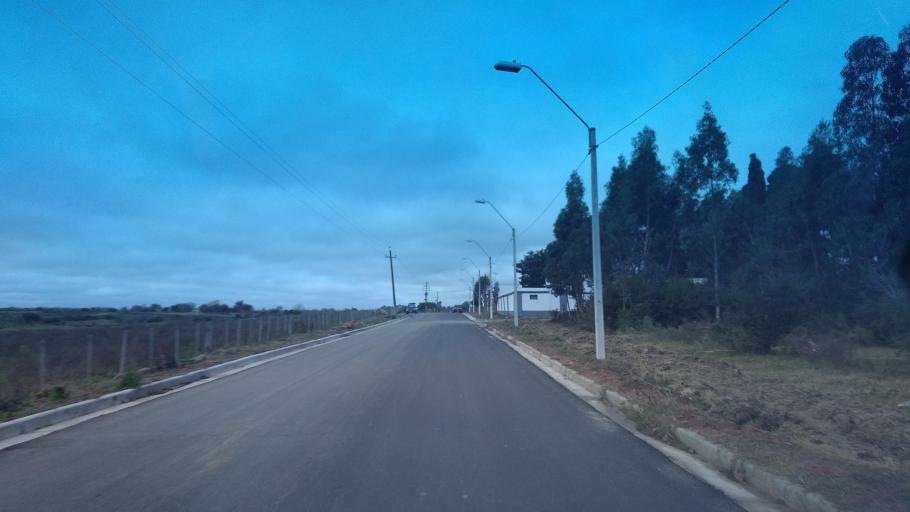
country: UY
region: Canelones
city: Tala
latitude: -34.2036
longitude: -55.7401
